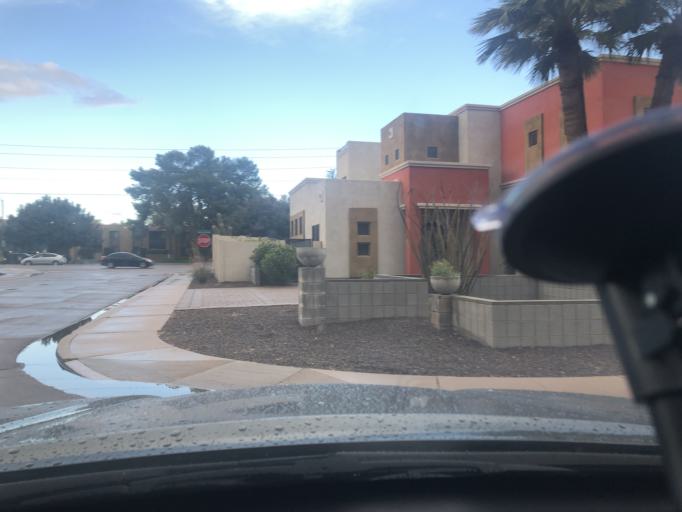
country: US
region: Arizona
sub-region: Maricopa County
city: Scottsdale
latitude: 33.4943
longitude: -111.8980
